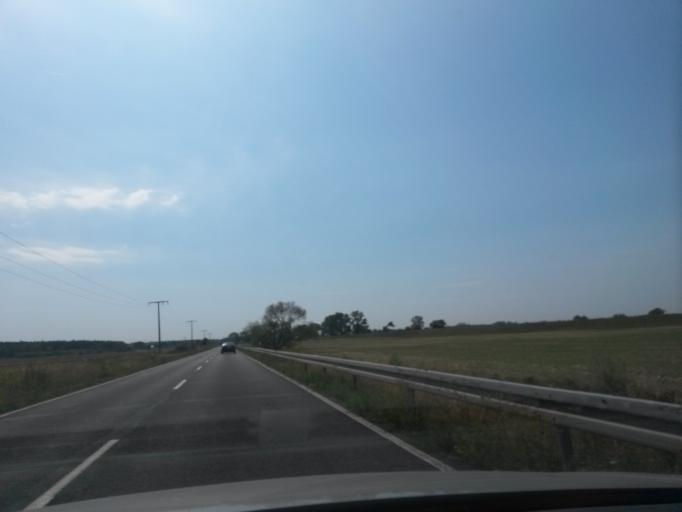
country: DE
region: Saxony-Anhalt
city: Jerichow
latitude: 52.4578
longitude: 12.0097
